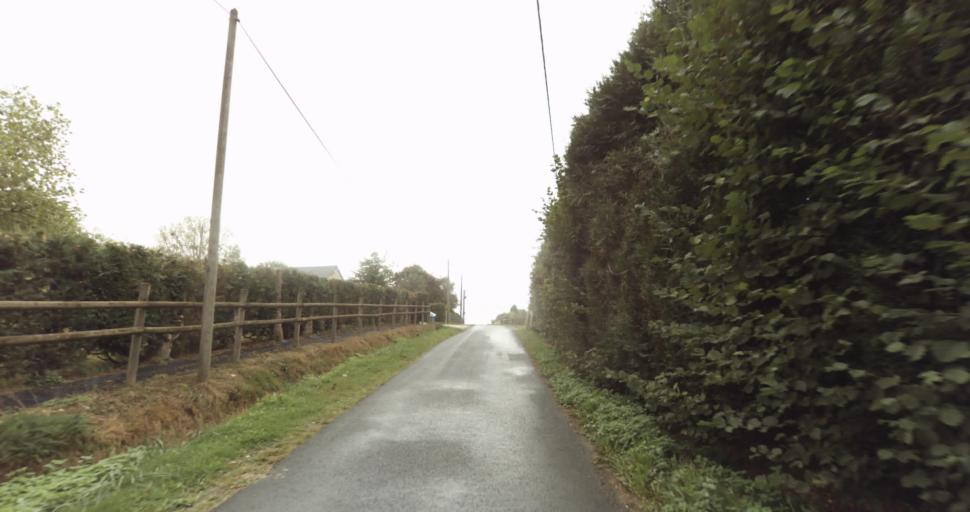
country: FR
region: Lower Normandy
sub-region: Departement de l'Orne
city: Sainte-Gauburge-Sainte-Colombe
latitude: 48.7372
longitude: 0.4755
